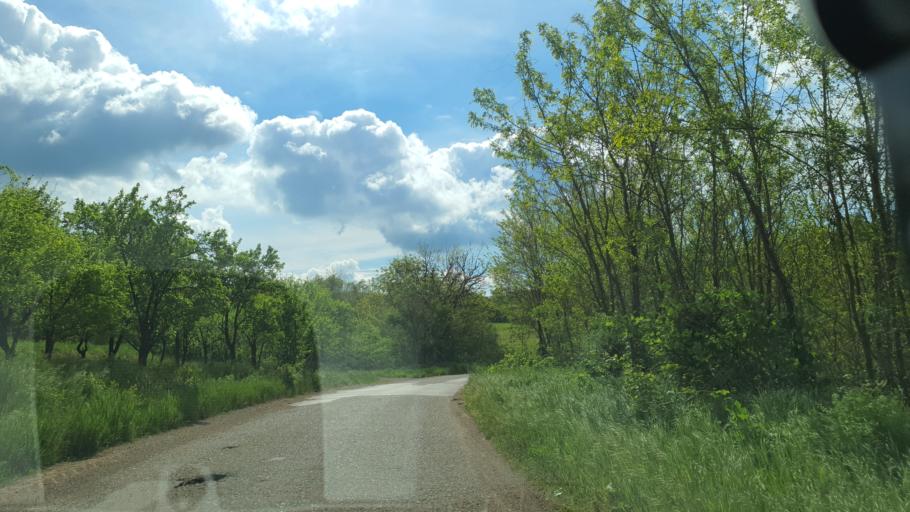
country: RS
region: Central Serbia
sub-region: Pomoravski Okrug
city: Cuprija
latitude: 43.9541
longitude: 21.4827
